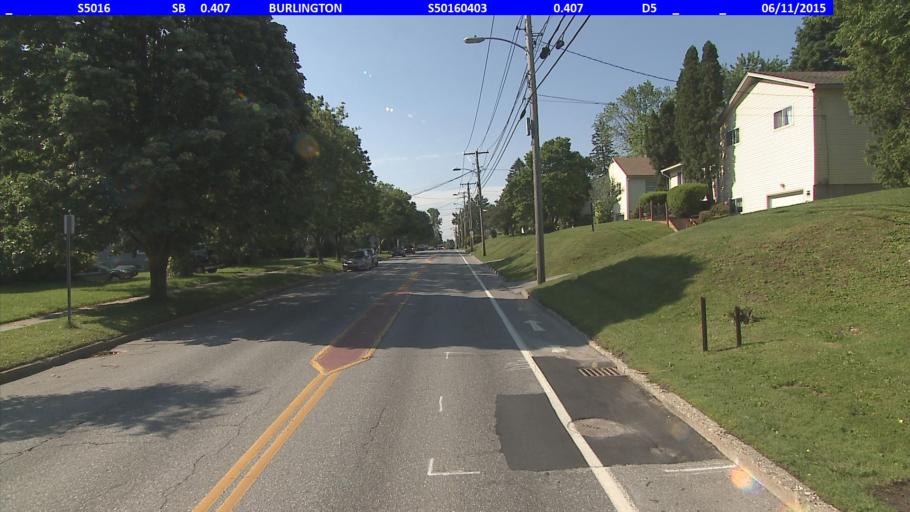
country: US
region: Vermont
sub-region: Chittenden County
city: Winooski
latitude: 44.4784
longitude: -73.1917
